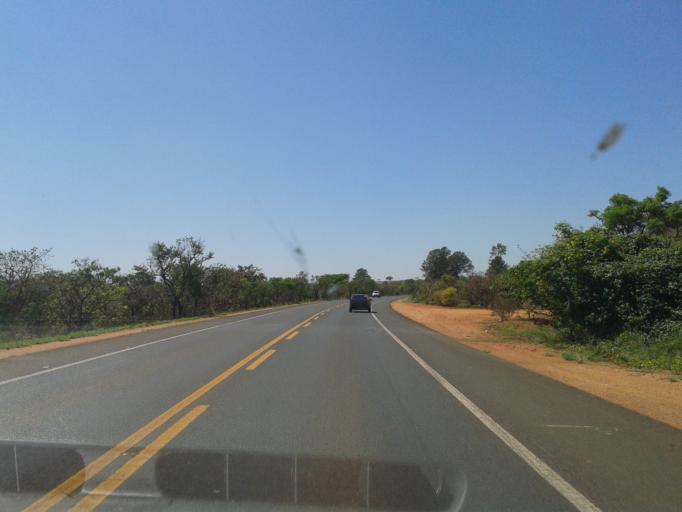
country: BR
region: Minas Gerais
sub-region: Uberaba
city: Uberaba
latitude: -19.2909
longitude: -47.6033
